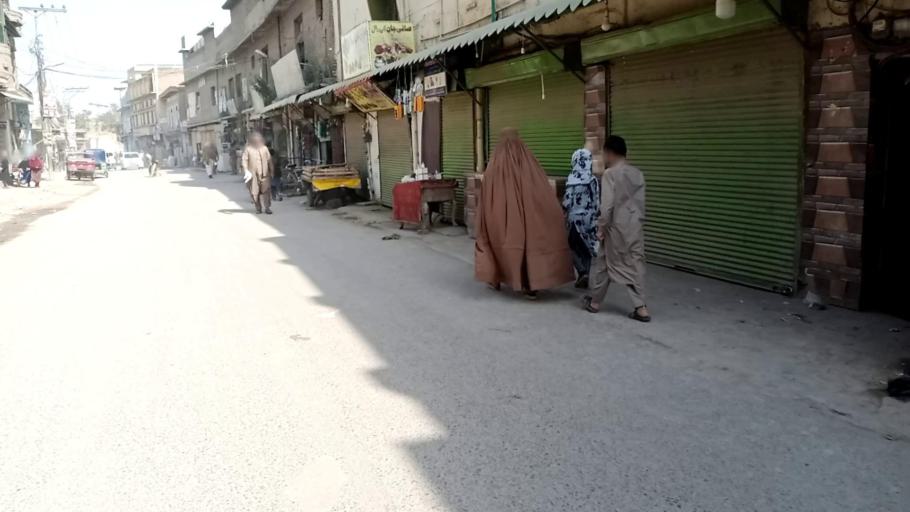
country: PK
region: Khyber Pakhtunkhwa
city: Peshawar
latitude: 33.9962
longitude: 71.5786
